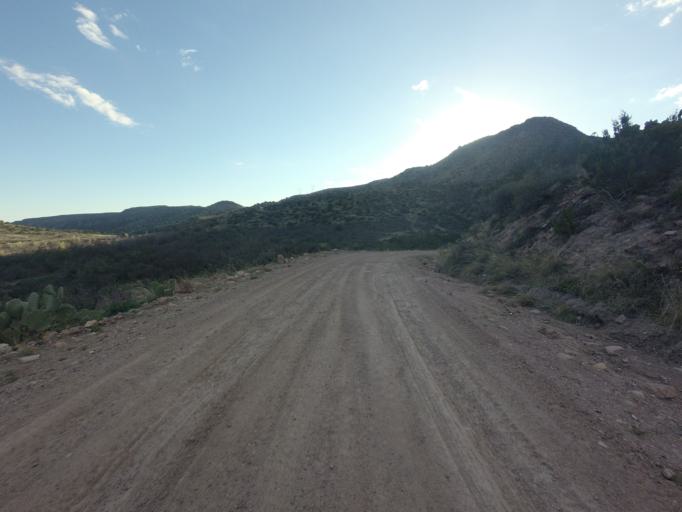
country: US
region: Arizona
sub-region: Gila County
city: Pine
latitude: 34.3707
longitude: -111.6666
